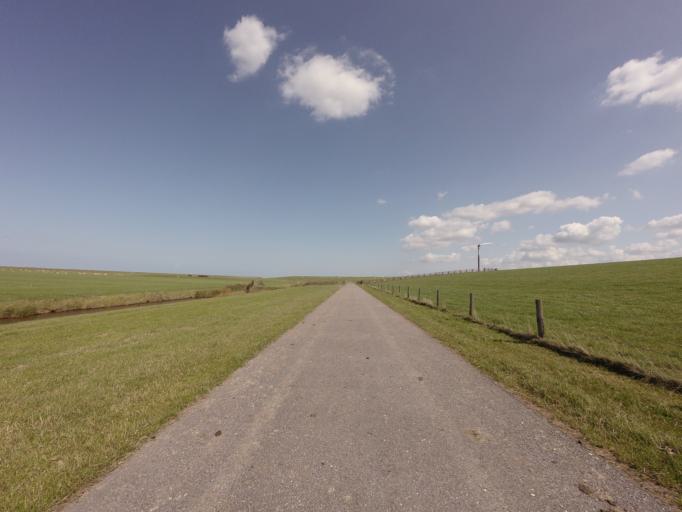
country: NL
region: Friesland
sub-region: Gemeente Ferwerderadiel
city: Marrum
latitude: 53.3332
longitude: 5.7781
